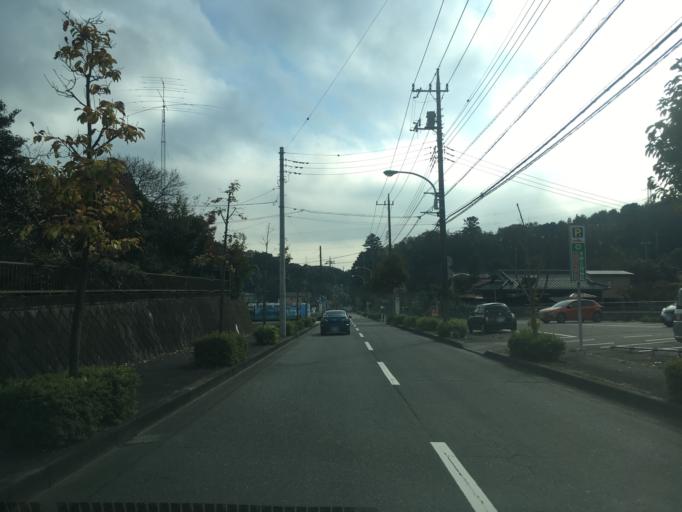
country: JP
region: Tokyo
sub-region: Machida-shi
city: Machida
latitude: 35.6037
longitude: 139.4208
